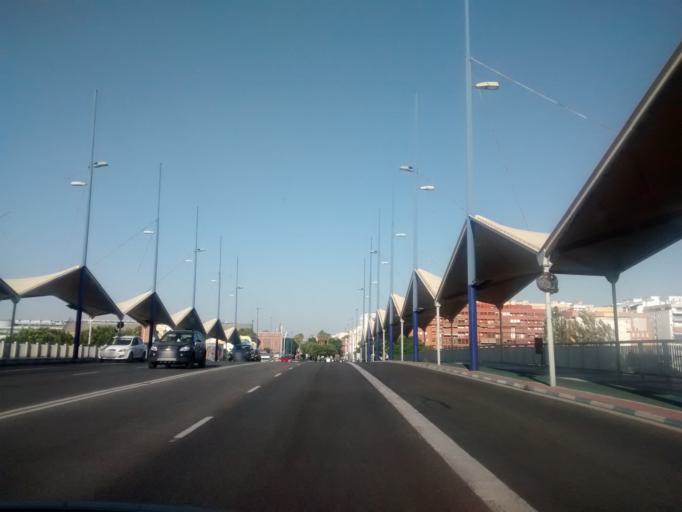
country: ES
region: Andalusia
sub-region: Provincia de Sevilla
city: Camas
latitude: 37.3903
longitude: -6.0068
